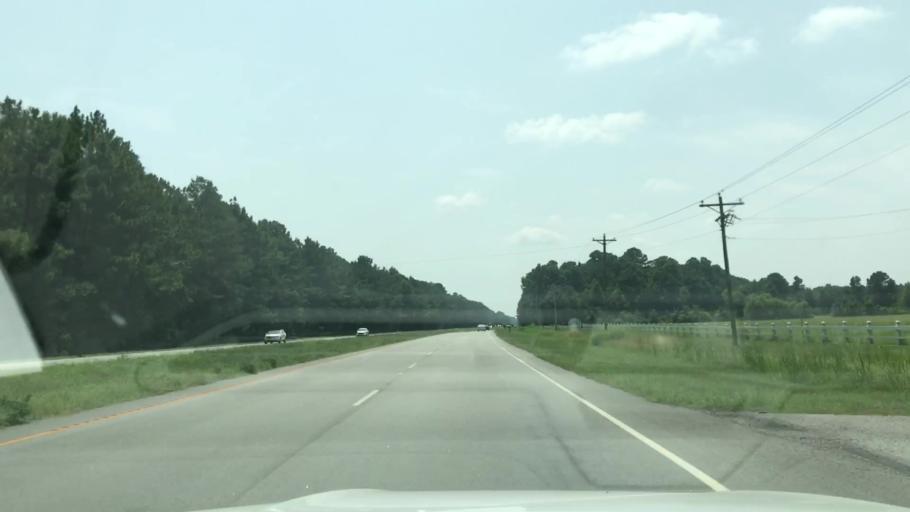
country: US
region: South Carolina
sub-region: Charleston County
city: Awendaw
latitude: 33.1254
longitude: -79.4498
